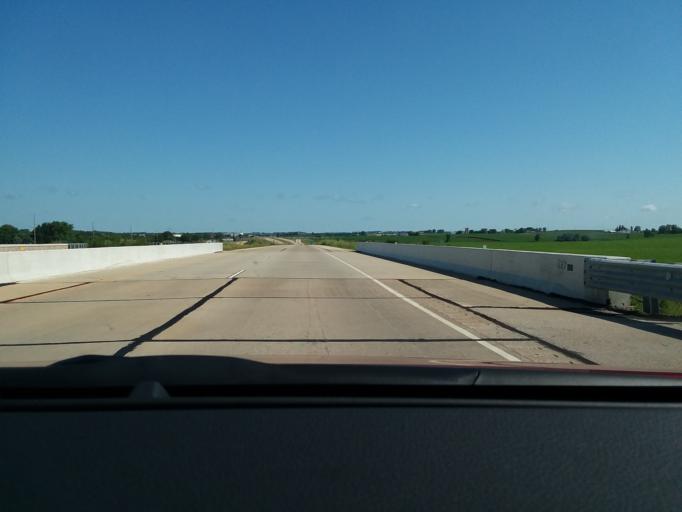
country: US
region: Wisconsin
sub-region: Dane County
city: De Forest
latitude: 43.2380
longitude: -89.3225
